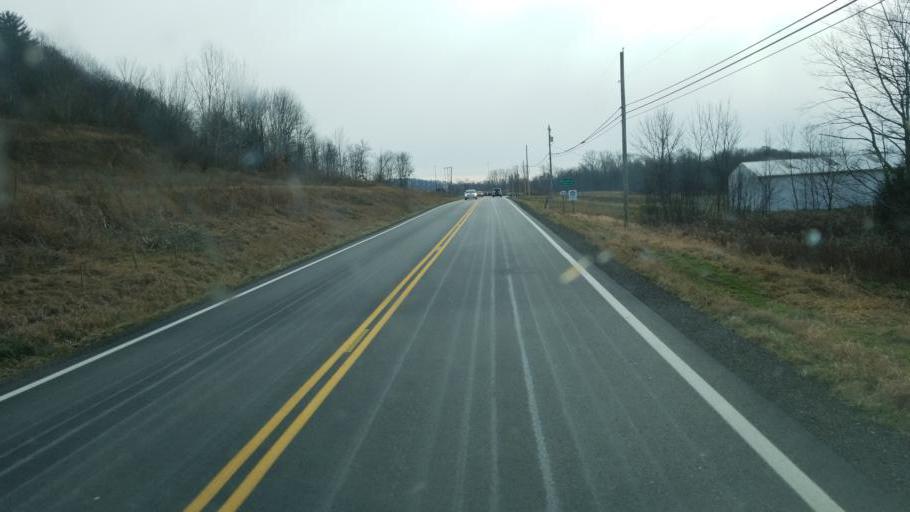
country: US
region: Ohio
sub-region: Richland County
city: Lexington
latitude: 40.6571
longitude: -82.5493
